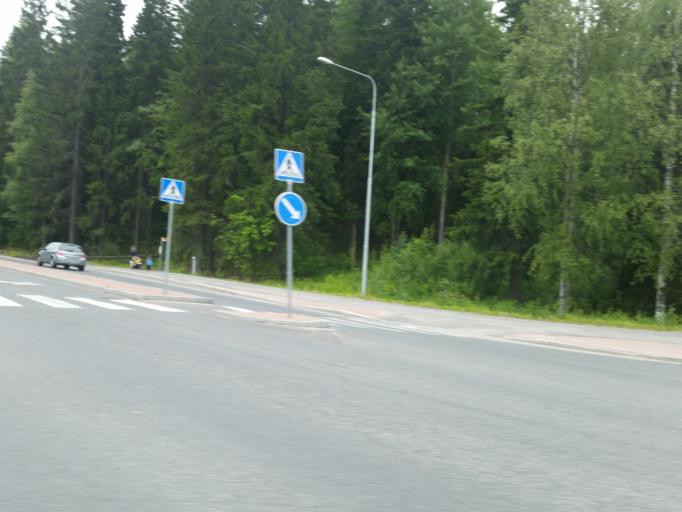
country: FI
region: Northern Savo
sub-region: Kuopio
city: Kuopio
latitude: 62.8708
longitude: 27.6252
